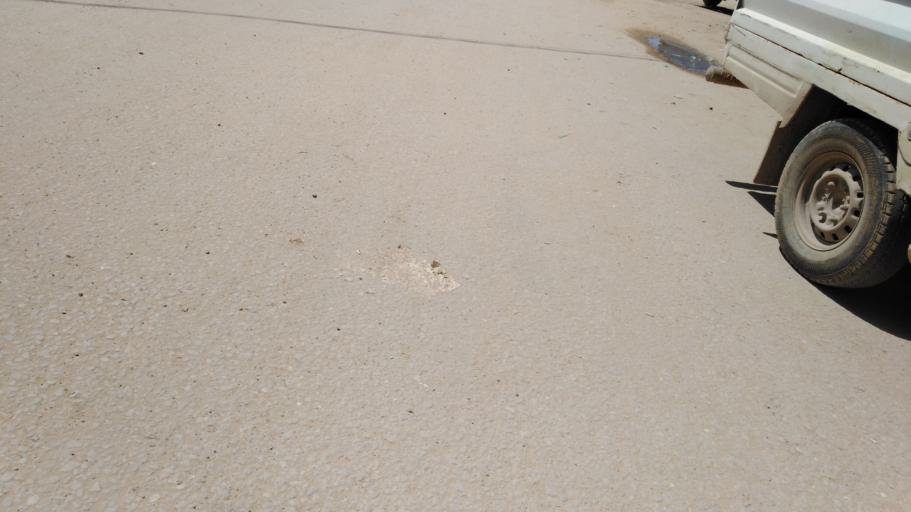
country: TN
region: Safaqis
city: Sfax
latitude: 34.7404
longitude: 10.5306
